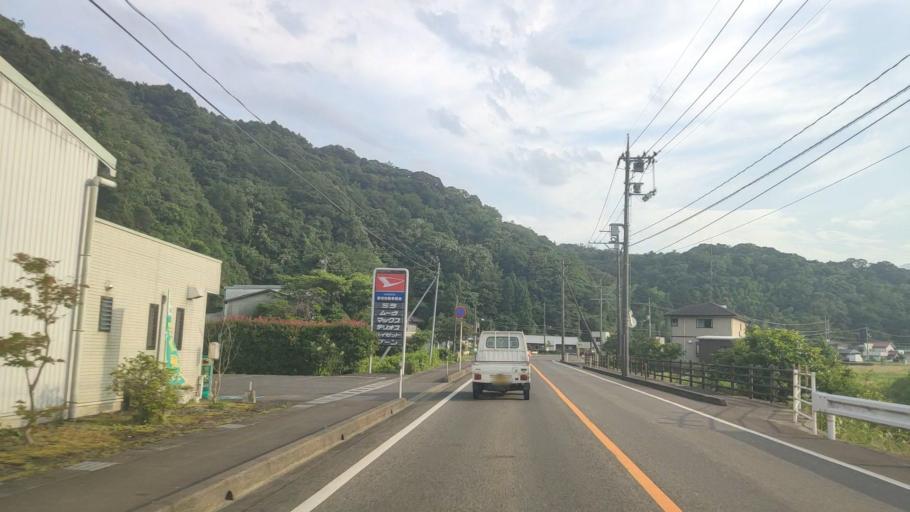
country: JP
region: Tottori
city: Kurayoshi
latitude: 35.3705
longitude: 133.7674
